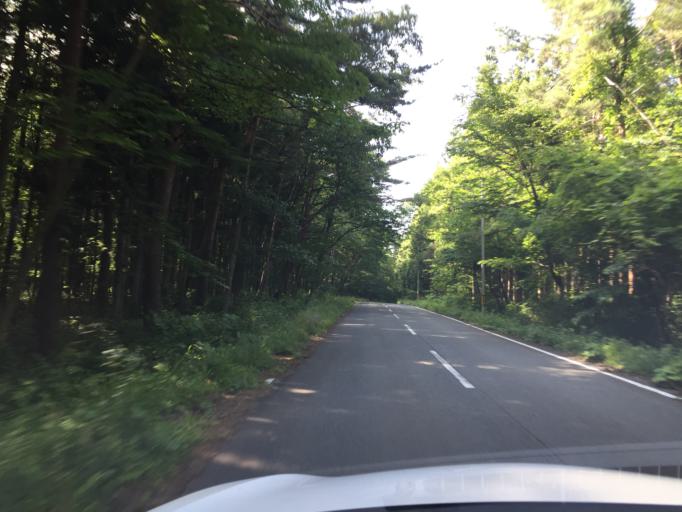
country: JP
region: Fukushima
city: Ishikawa
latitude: 37.1544
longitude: 140.6325
